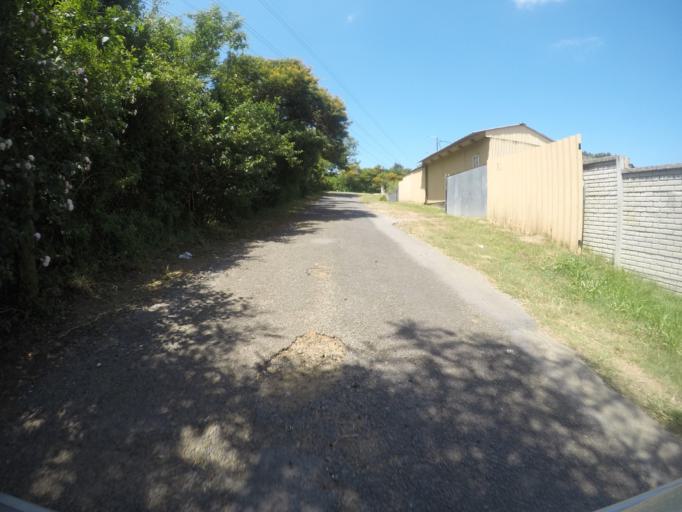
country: ZA
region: Eastern Cape
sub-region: Buffalo City Metropolitan Municipality
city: East London
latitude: -32.9678
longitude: 27.8537
